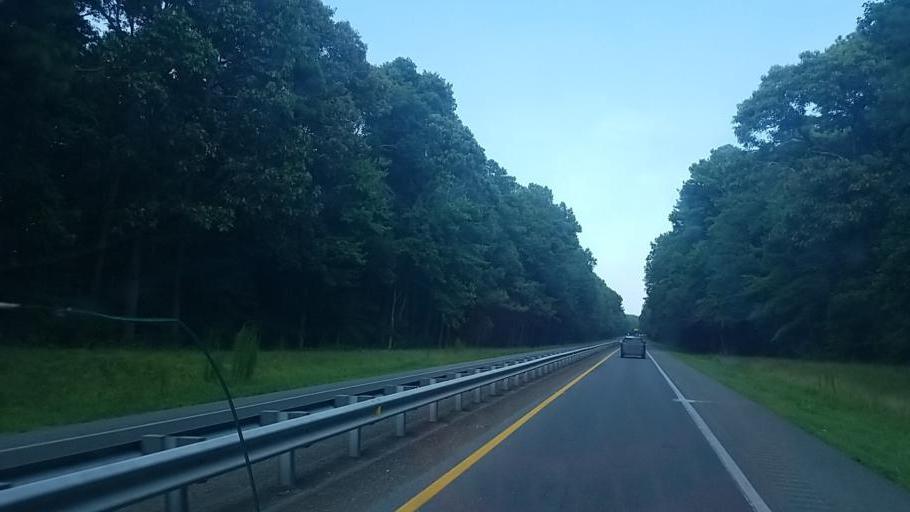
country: US
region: Maryland
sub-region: Worcester County
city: Ocean Pines
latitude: 38.3841
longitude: -75.1591
